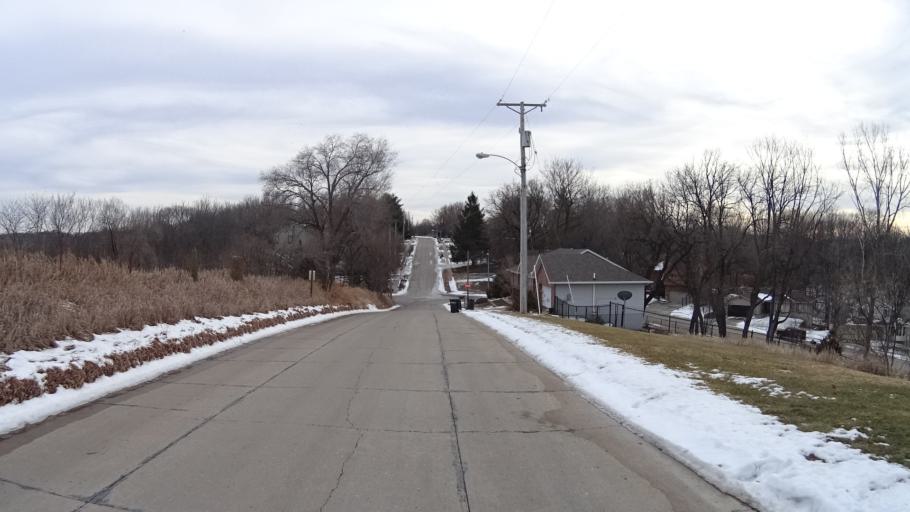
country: US
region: Nebraska
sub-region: Sarpy County
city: Bellevue
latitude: 41.1756
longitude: -95.9112
